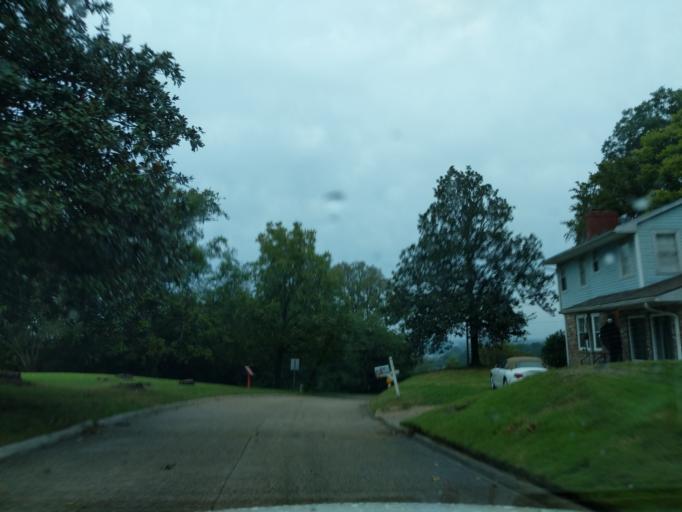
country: US
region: Mississippi
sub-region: Warren County
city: Vicksburg
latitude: 32.3674
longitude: -90.8710
